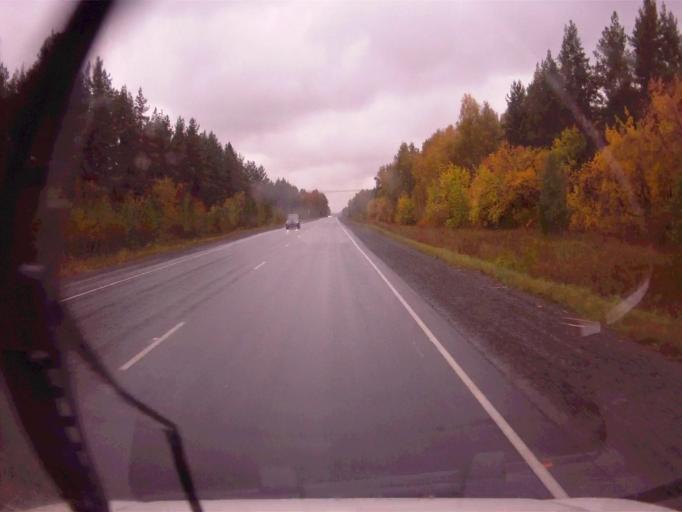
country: RU
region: Chelyabinsk
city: Roshchino
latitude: 55.3801
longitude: 61.1425
